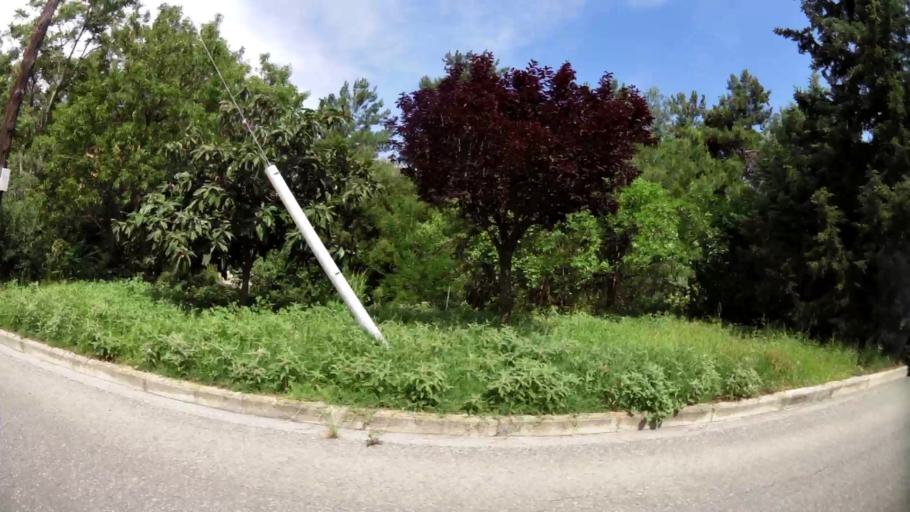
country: GR
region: Central Macedonia
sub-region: Nomos Thessalonikis
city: Panorama
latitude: 40.5895
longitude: 23.0184
